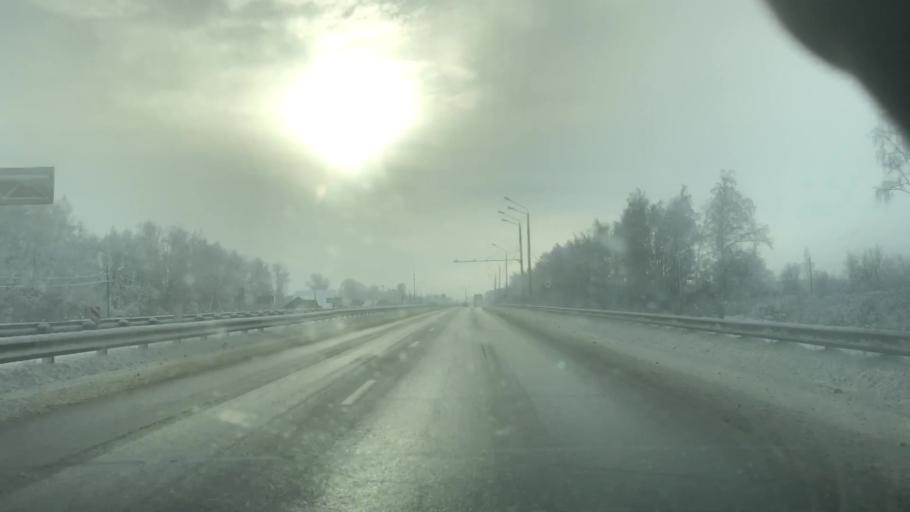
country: RU
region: Tula
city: Venev
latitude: 54.3473
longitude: 38.1543
